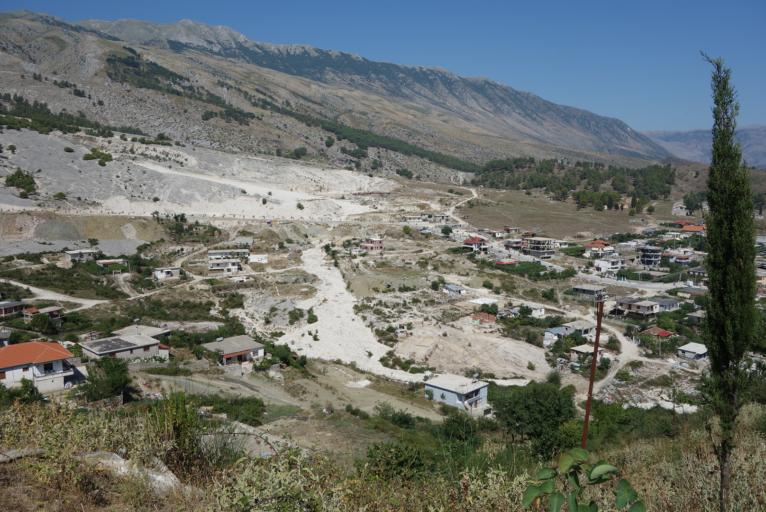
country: AL
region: Gjirokaster
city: Gjirokaster
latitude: 40.0842
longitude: 20.1364
